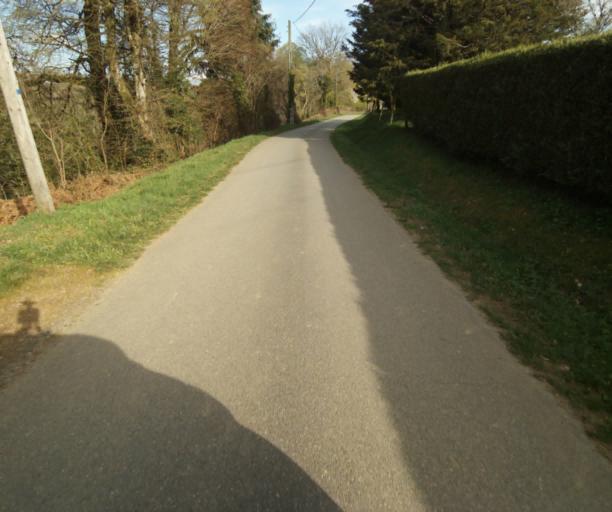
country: FR
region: Limousin
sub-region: Departement de la Correze
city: Naves
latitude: 45.3059
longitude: 1.7503
